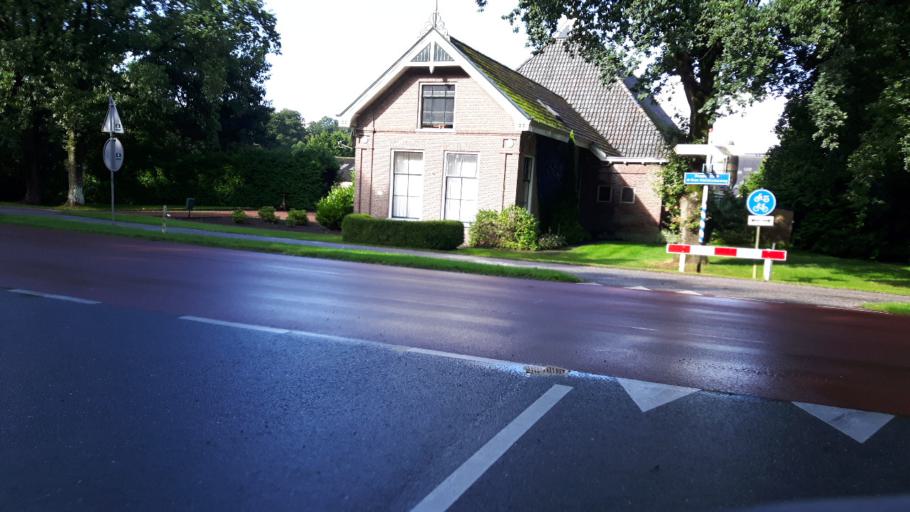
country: NL
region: Friesland
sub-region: Gemeente Smallingerland
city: Drachten
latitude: 53.0683
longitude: 6.1056
